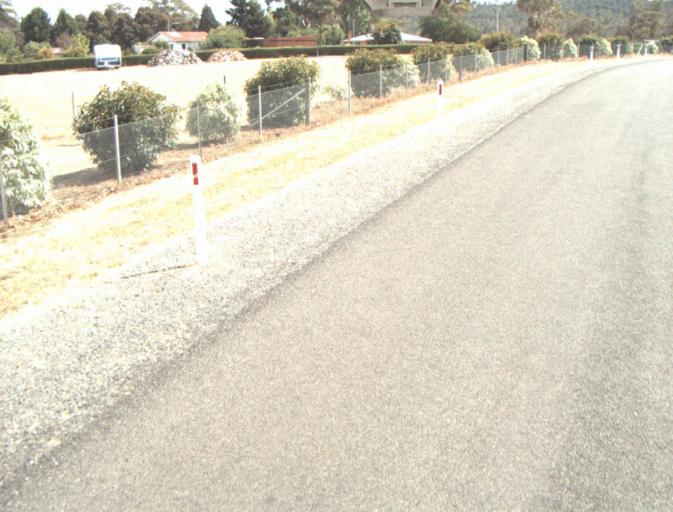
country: AU
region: Tasmania
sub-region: Launceston
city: Mayfield
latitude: -41.3419
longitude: 147.0863
